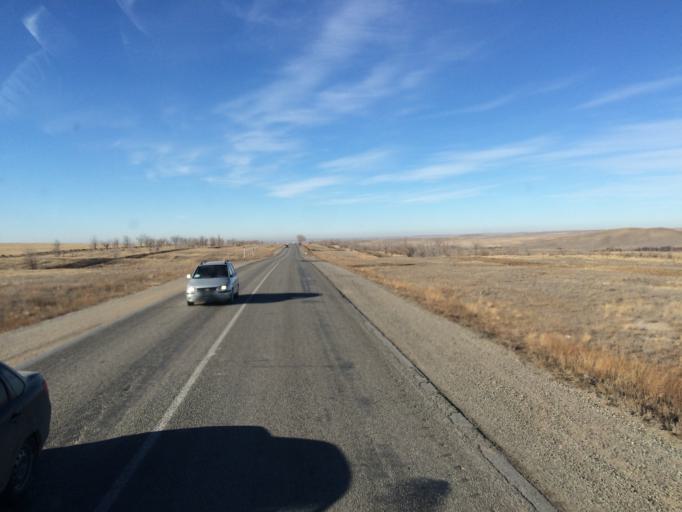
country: KZ
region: Aqtoebe
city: Aqtobe
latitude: 50.2821
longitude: 57.7458
